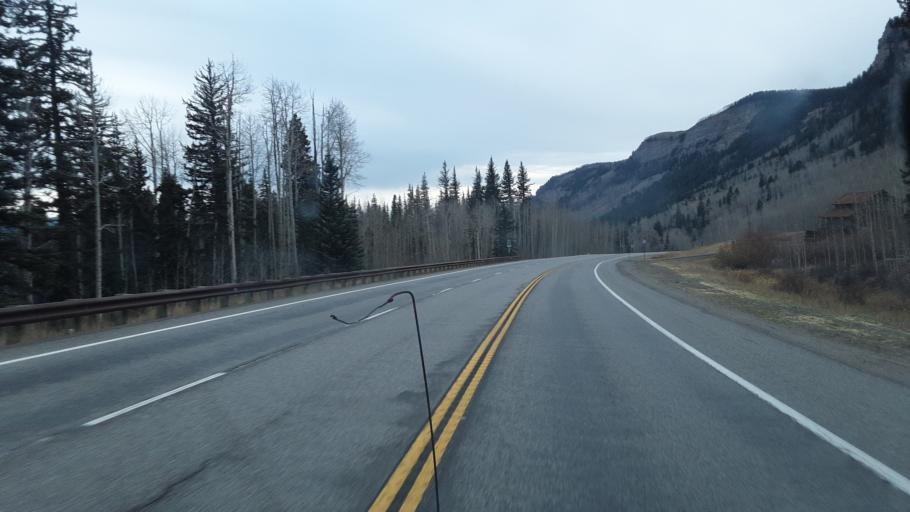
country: US
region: Colorado
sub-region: San Juan County
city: Silverton
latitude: 37.5750
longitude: -107.8225
